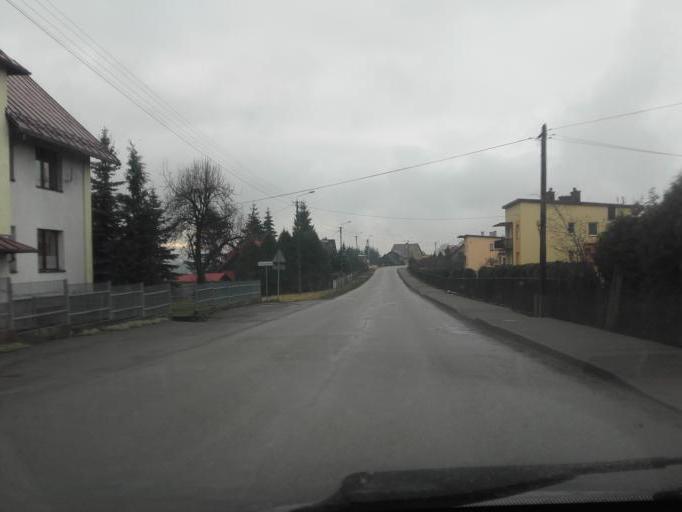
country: PL
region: Silesian Voivodeship
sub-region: Powiat cieszynski
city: Koniakow
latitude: 49.5507
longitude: 18.9384
